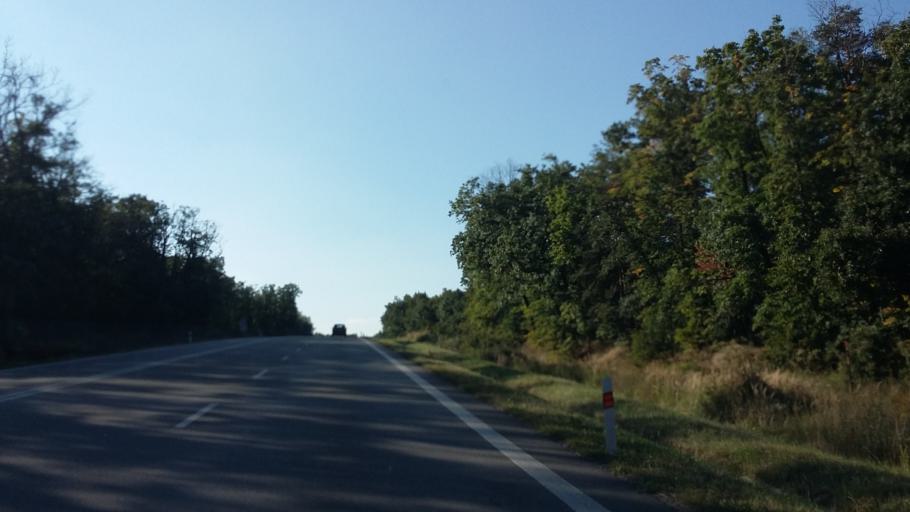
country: CZ
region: South Moravian
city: Troubsko
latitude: 49.1856
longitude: 16.4734
